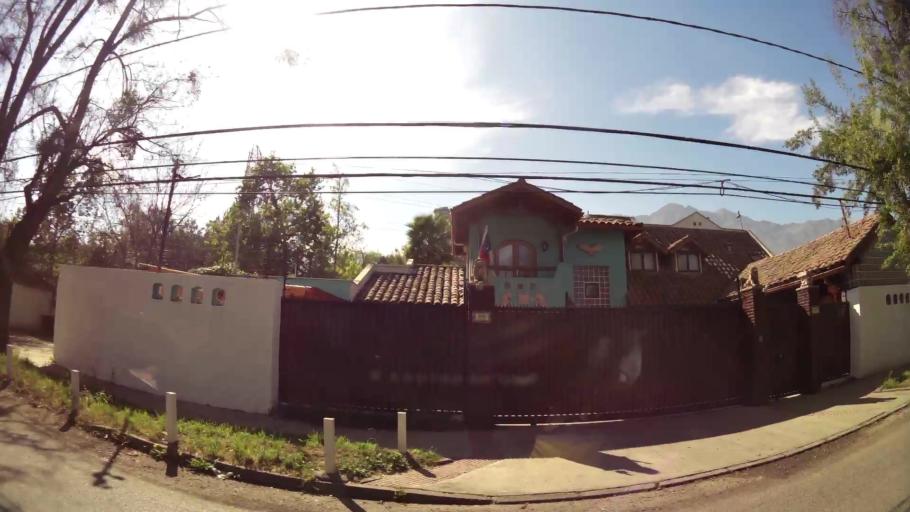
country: CL
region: Santiago Metropolitan
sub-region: Provincia de Santiago
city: Villa Presidente Frei, Nunoa, Santiago, Chile
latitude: -33.4487
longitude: -70.5282
